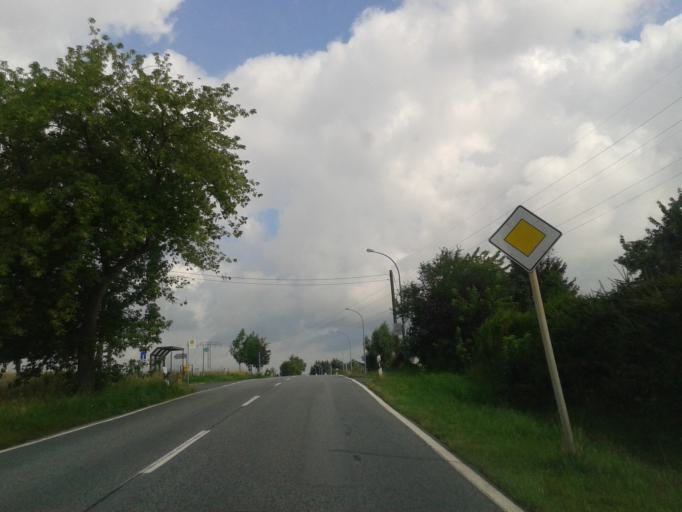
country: DE
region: Saxony
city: Radeberg
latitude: 51.0547
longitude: 13.9359
